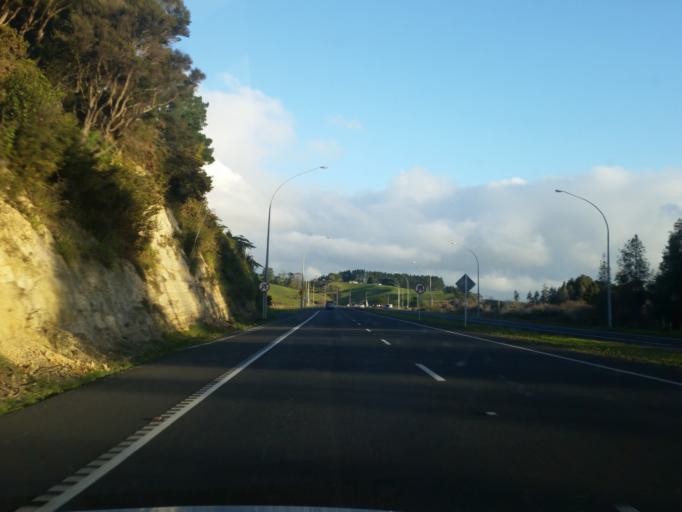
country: NZ
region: Waikato
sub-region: Waikato District
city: Te Kauwhata
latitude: -37.3230
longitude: 175.0664
